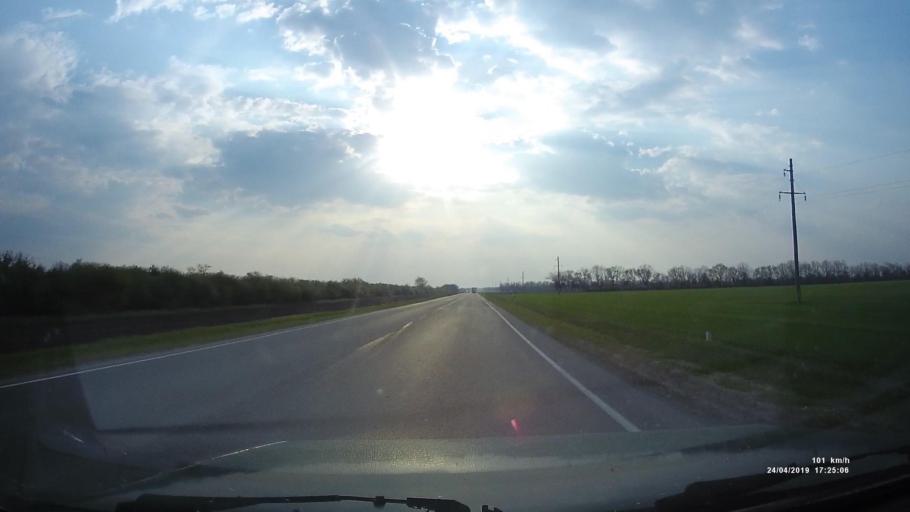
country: RU
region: Rostov
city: Gigant
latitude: 46.5249
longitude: 41.2474
